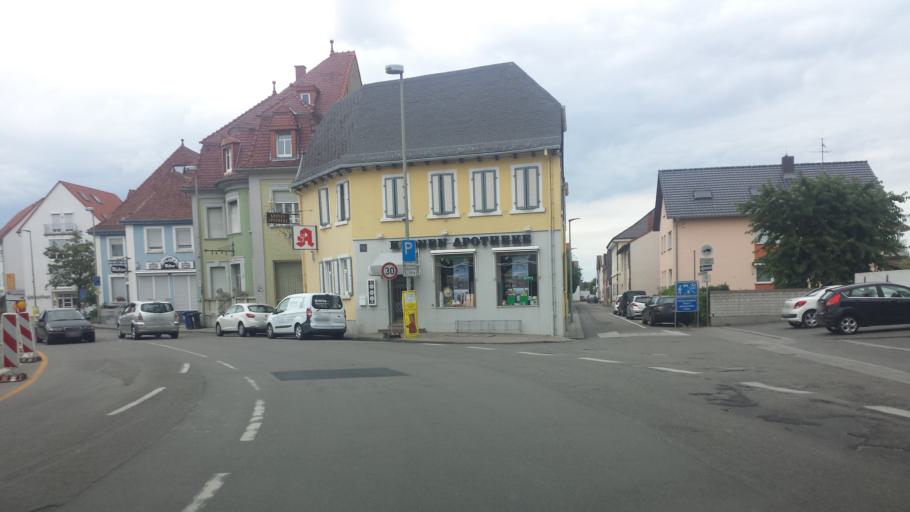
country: DE
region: Rheinland-Pfalz
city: Mutterstadt
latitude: 49.4424
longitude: 8.3558
